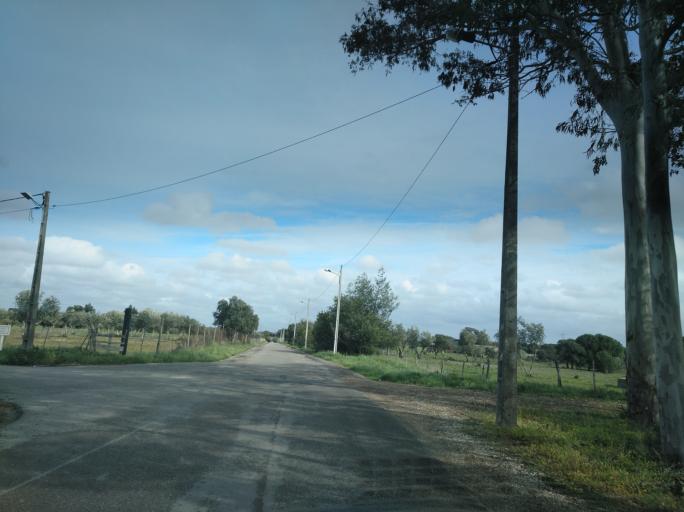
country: PT
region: Setubal
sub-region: Grandola
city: Grandola
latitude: 38.1877
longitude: -8.5609
